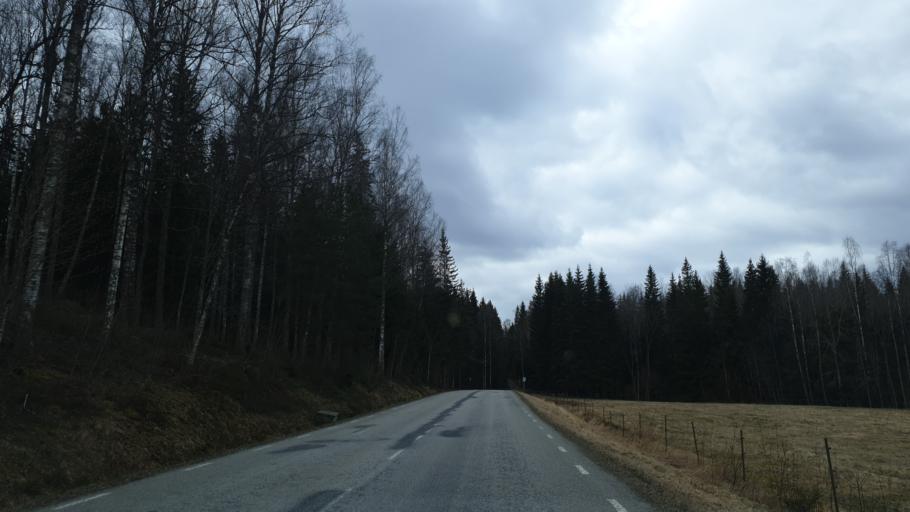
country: SE
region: OErebro
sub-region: Nora Kommun
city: As
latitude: 59.5614
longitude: 15.0129
